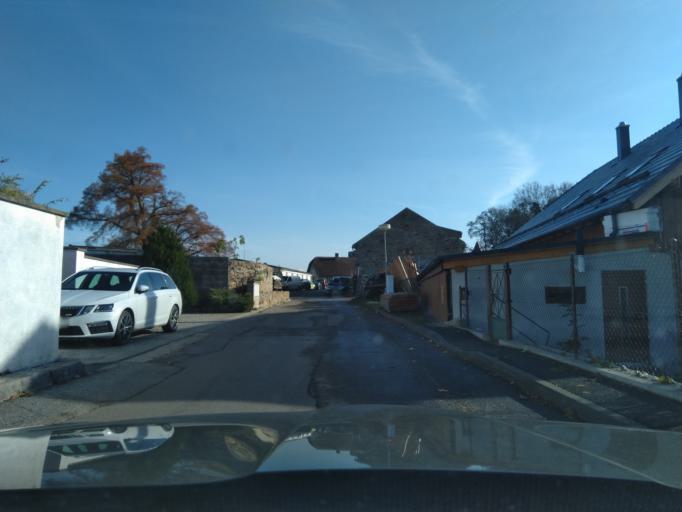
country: CZ
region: Jihocesky
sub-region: Okres Prachatice
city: Vimperk
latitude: 49.0562
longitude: 13.7699
